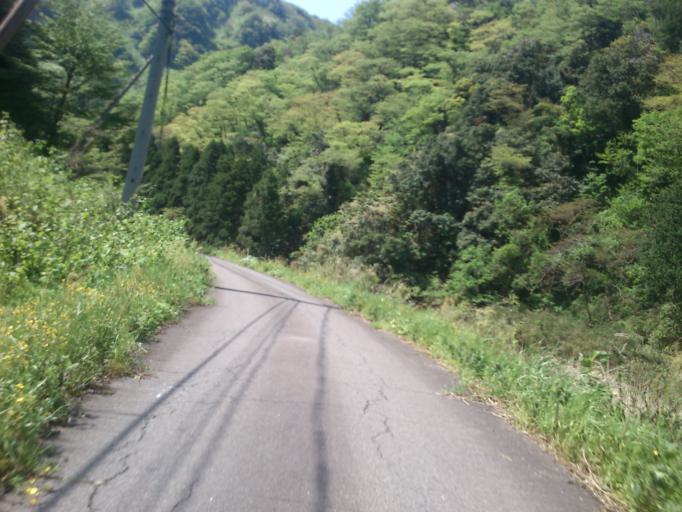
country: JP
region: Kyoto
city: Miyazu
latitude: 35.7238
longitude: 135.1619
